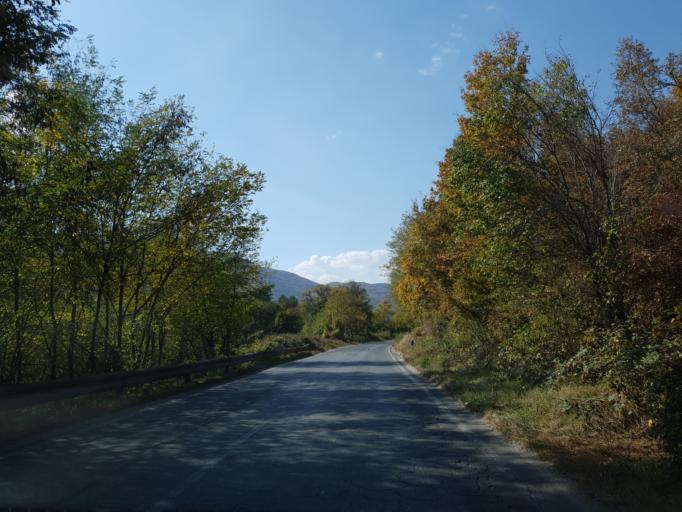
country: MK
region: Vranestica
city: Vranestica
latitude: 41.4684
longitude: 21.0158
